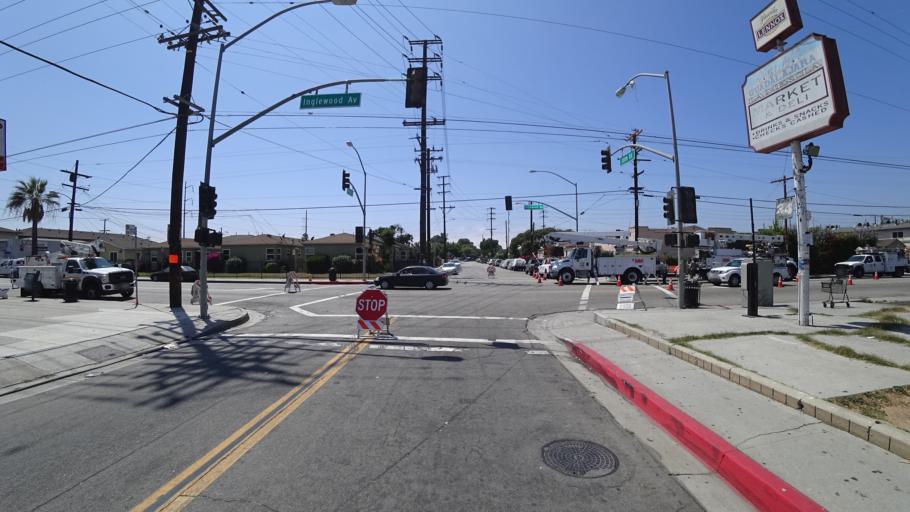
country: US
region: California
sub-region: Los Angeles County
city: Lennox
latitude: 33.9345
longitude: -118.3611
